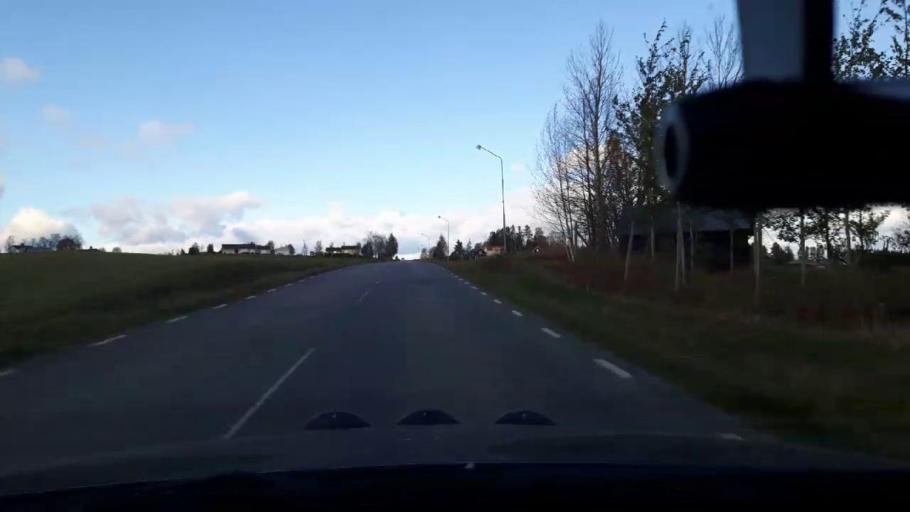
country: SE
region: Jaemtland
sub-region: Bergs Kommun
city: Hoverberg
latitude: 63.0044
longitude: 14.3400
